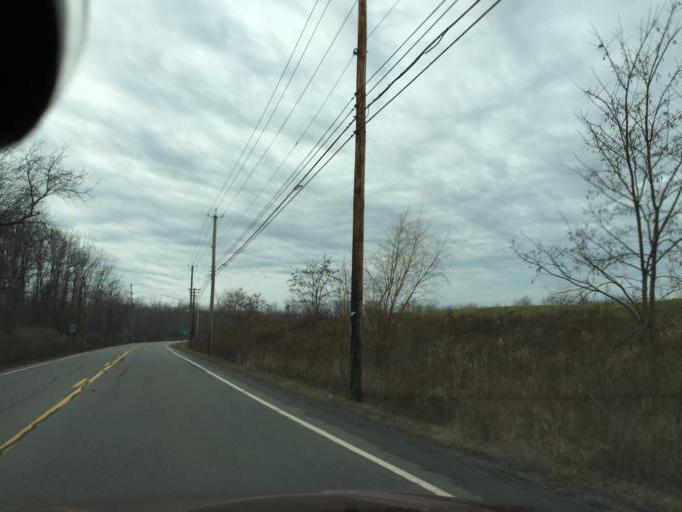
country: US
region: New York
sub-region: Monroe County
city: Scottsville
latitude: 43.0893
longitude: -77.7217
